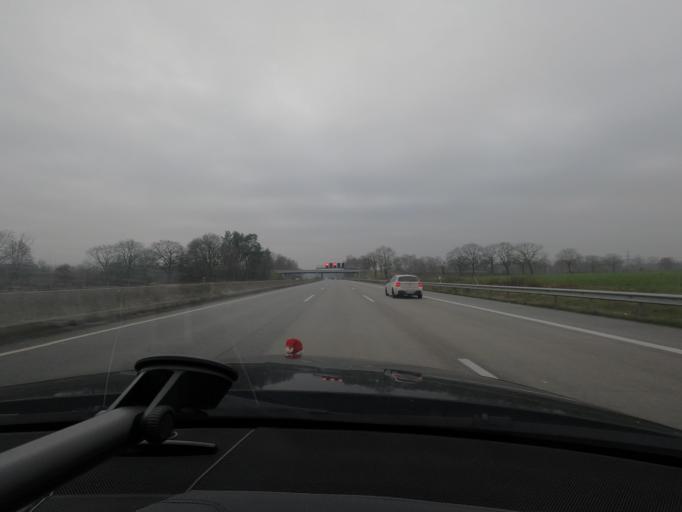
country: DE
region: Schleswig-Holstein
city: Bonningstedt
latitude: 53.6637
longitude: 9.9354
